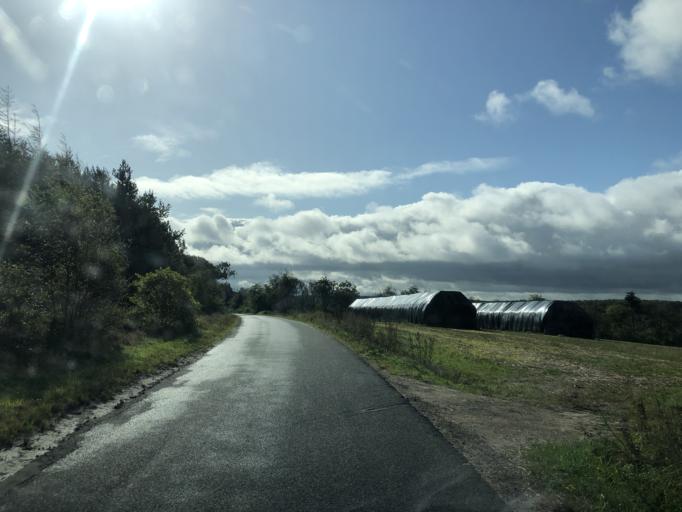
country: DK
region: Central Jutland
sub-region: Holstebro Kommune
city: Ulfborg
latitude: 56.2967
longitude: 8.4604
